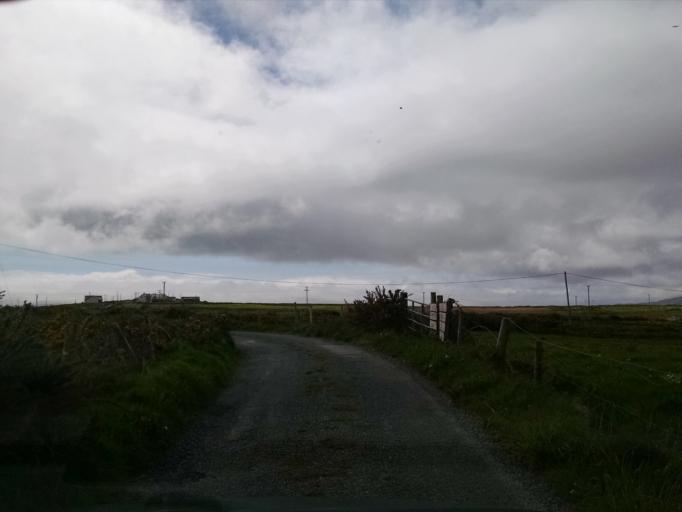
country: IE
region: Connaught
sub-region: County Galway
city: Clifden
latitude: 53.7540
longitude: -9.8844
